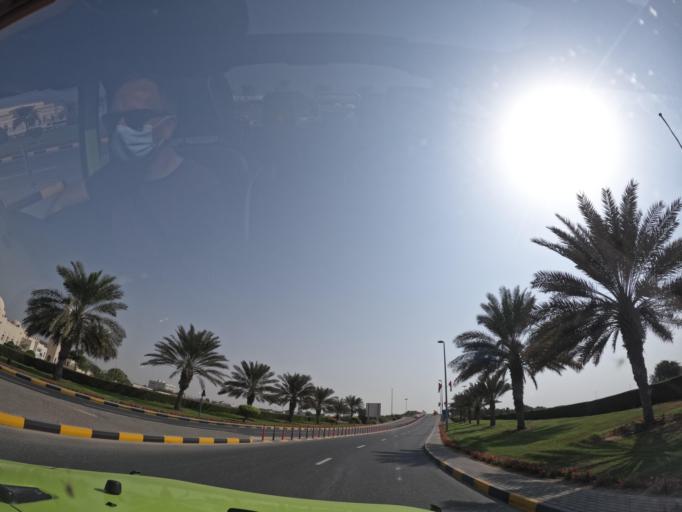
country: AE
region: Umm al Qaywayn
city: Umm al Qaywayn
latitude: 25.4790
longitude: 55.5224
